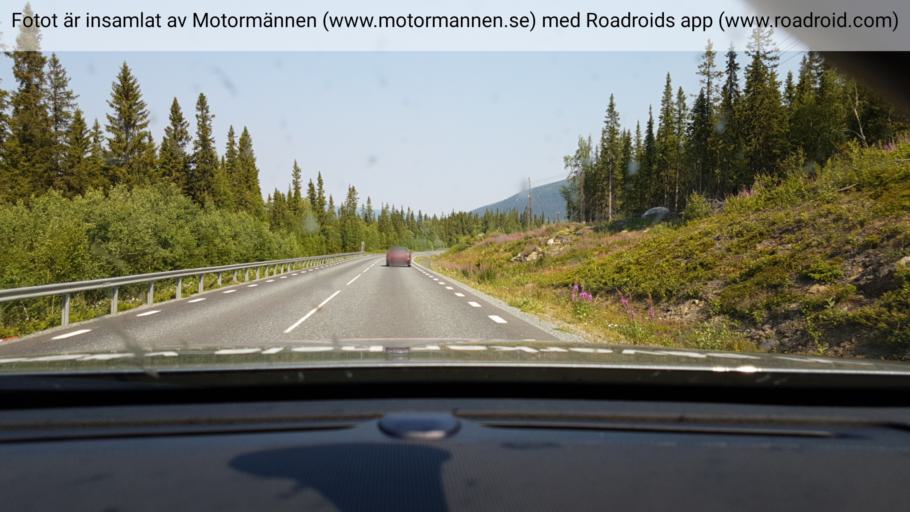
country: SE
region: Vaesterbotten
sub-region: Vilhelmina Kommun
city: Sjoberg
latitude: 65.6094
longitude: 15.5327
